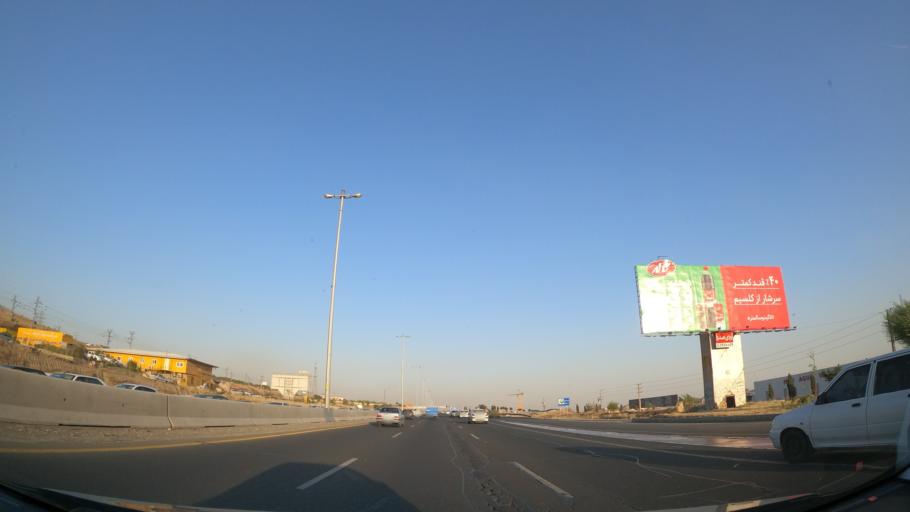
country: IR
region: Tehran
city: Shahr-e Qods
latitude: 35.7537
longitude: 51.0753
